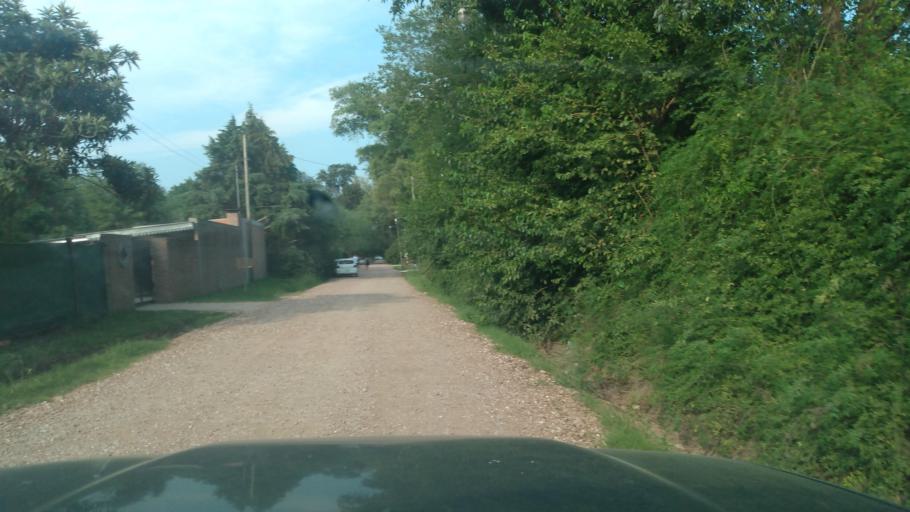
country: AR
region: Buenos Aires
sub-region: Partido de Lujan
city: Lujan
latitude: -34.5481
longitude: -59.1294
